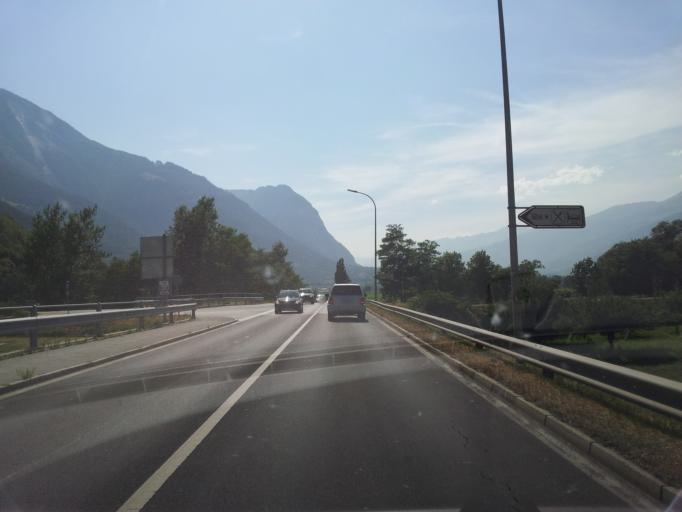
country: CH
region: Valais
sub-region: Leuk District
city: Turtmann
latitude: 46.3013
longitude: 7.6988
